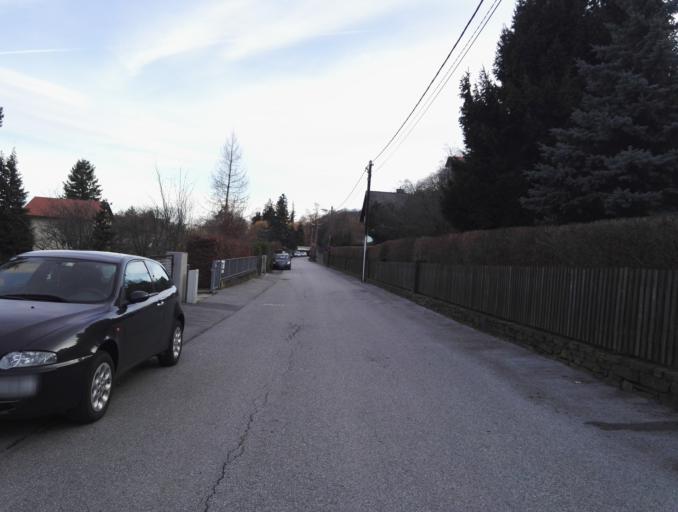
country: AT
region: Styria
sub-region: Graz Stadt
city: Goesting
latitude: 47.1025
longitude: 15.3935
